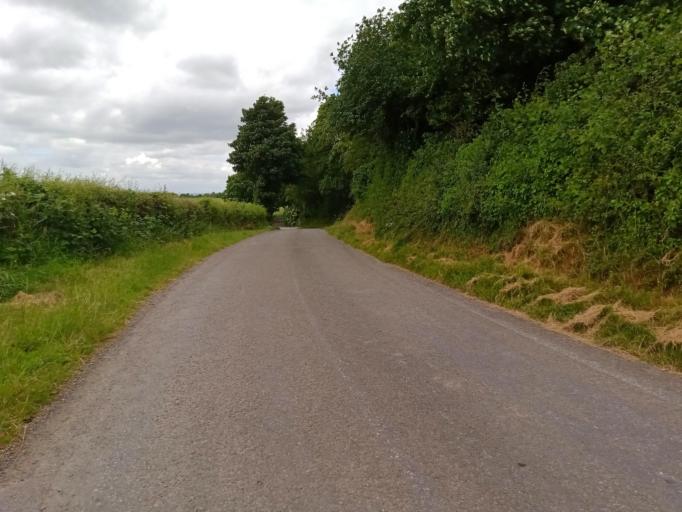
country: IE
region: Leinster
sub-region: Kilkenny
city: Kilkenny
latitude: 52.6797
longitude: -7.2438
